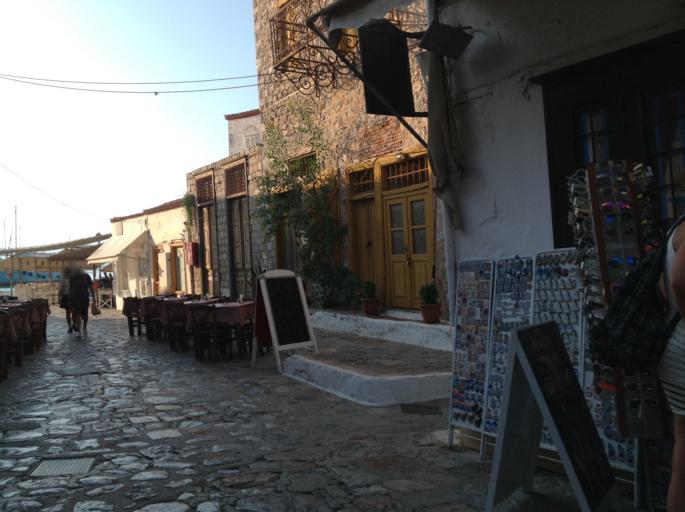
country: GR
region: Attica
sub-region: Nomos Piraios
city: Ydra
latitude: 37.3498
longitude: 23.4672
